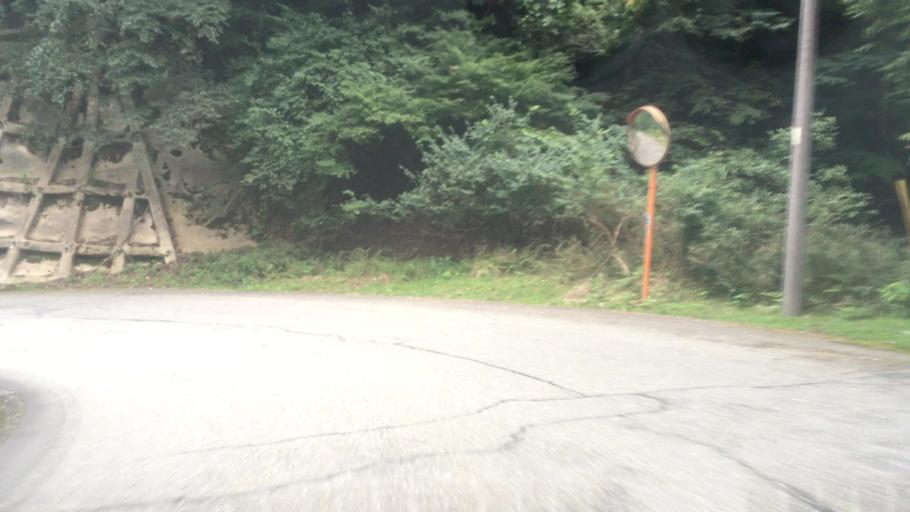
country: JP
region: Hyogo
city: Toyooka
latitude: 35.6103
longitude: 134.8355
